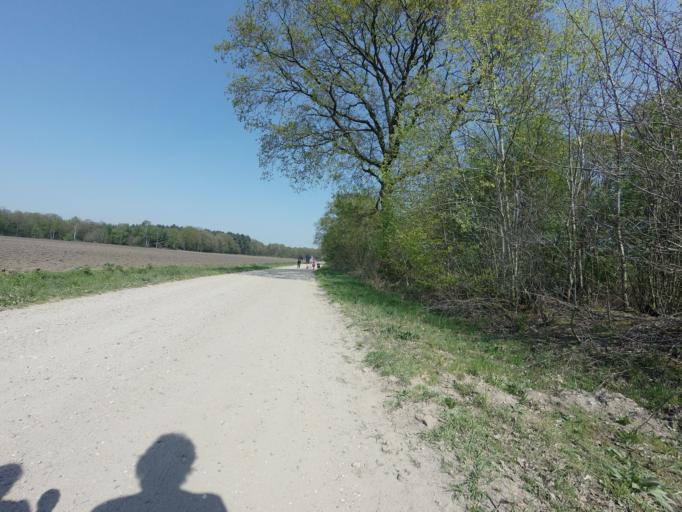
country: NL
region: North Brabant
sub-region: Gemeente Baarle-Nassau
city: Baarle-Nassau
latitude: 51.4938
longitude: 4.9924
